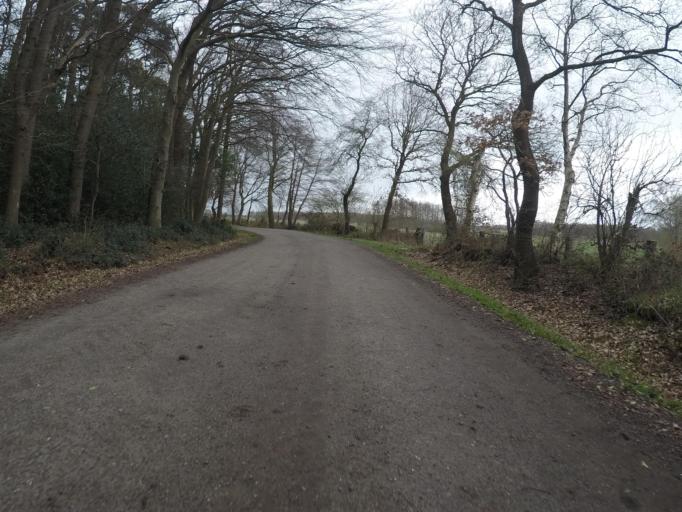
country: DE
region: Lower Saxony
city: Elmlohe
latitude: 53.6003
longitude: 8.6738
